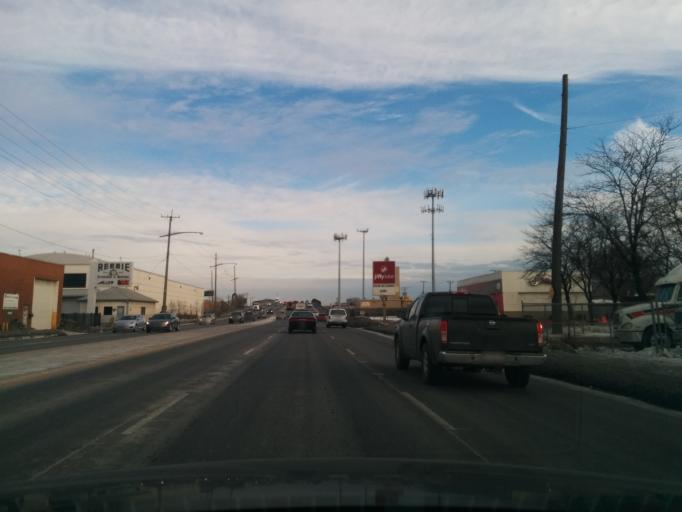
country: US
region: Illinois
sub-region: Cook County
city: Franklin Park
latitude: 41.9378
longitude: -87.8850
